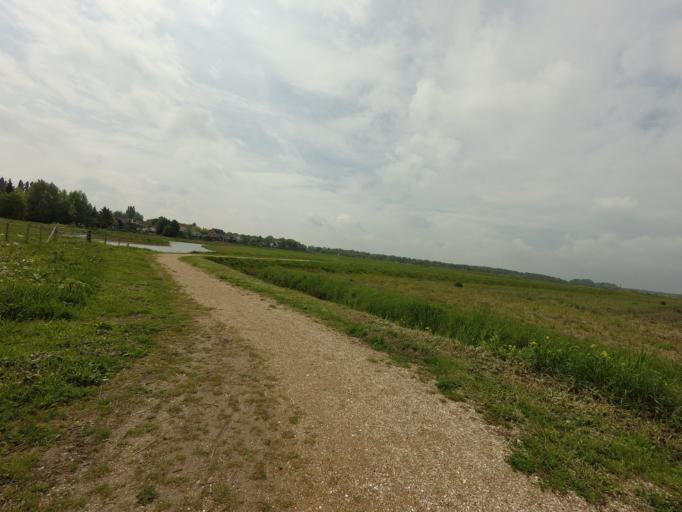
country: NL
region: South Holland
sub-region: Gemeente Zwijndrecht
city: Heerjansdam
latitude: 51.8413
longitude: 4.5579
